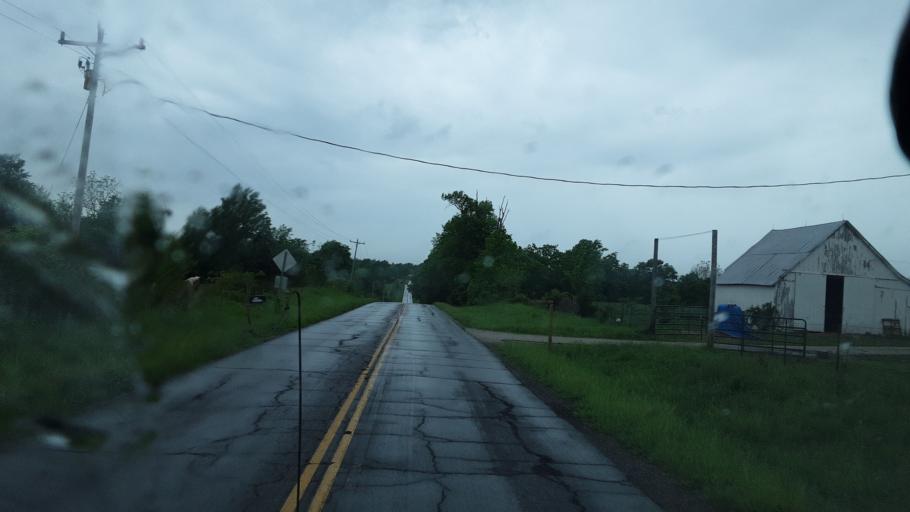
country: US
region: Missouri
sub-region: Boone County
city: Centralia
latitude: 39.3884
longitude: -92.2225
